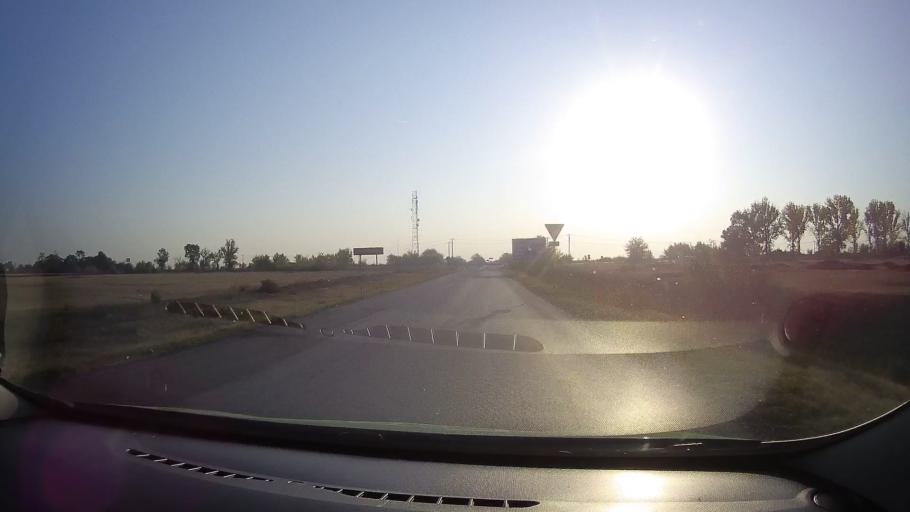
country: RO
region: Arad
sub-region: Comuna Zimandu Nou
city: Andrei Saguna
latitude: 46.3551
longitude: 21.4217
